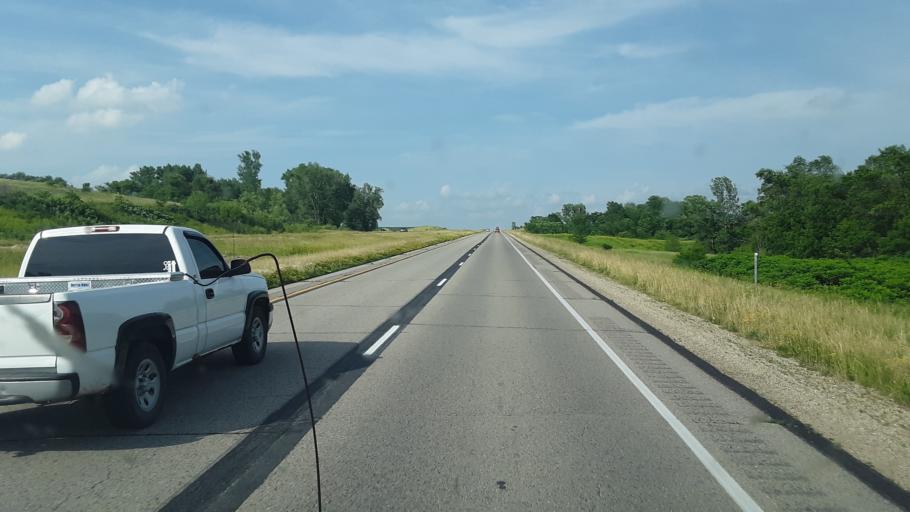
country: US
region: Iowa
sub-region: Jasper County
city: Baxter
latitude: 41.8958
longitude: -93.1854
